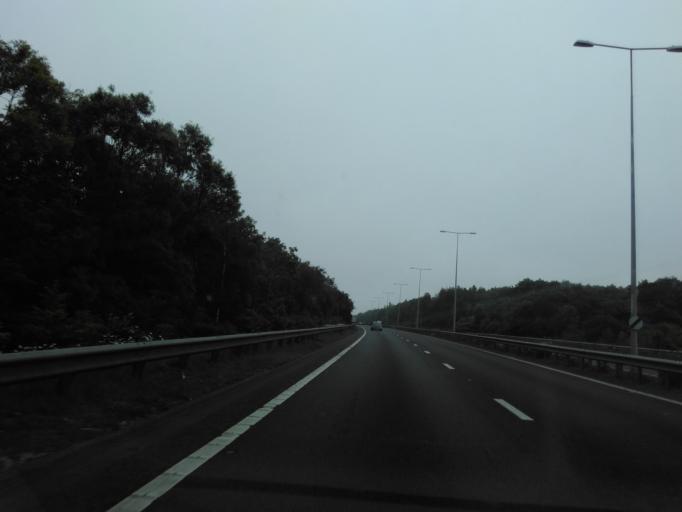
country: GB
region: England
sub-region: Kent
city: Dunkirk
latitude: 51.2901
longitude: 0.9647
